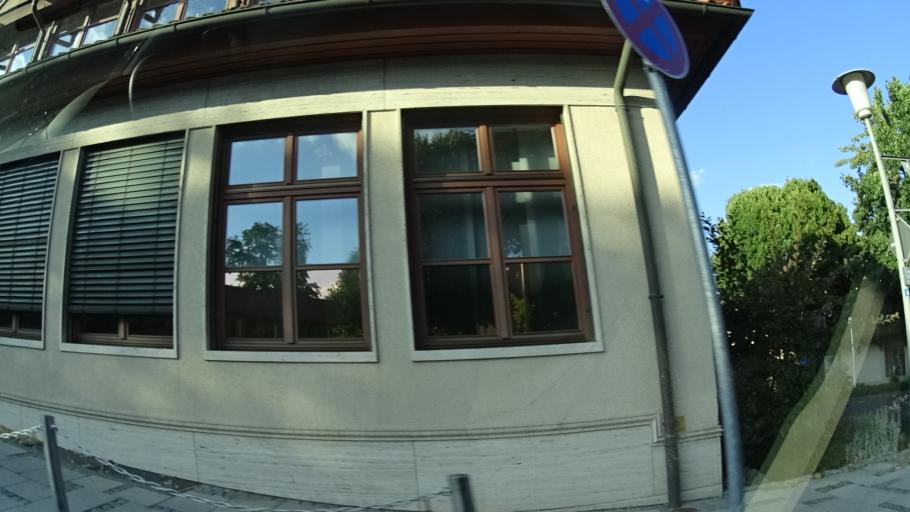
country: DE
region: Bavaria
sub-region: Regierungsbezirk Unterfranken
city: Mellrichstadt
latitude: 50.4298
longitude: 10.3063
